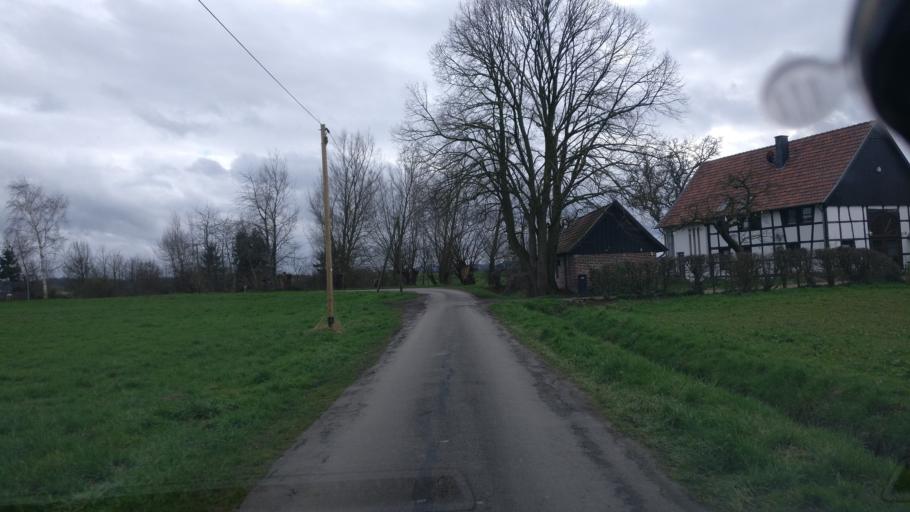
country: DE
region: North Rhine-Westphalia
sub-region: Regierungsbezirk Detmold
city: Lage
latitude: 52.0253
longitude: 8.7759
